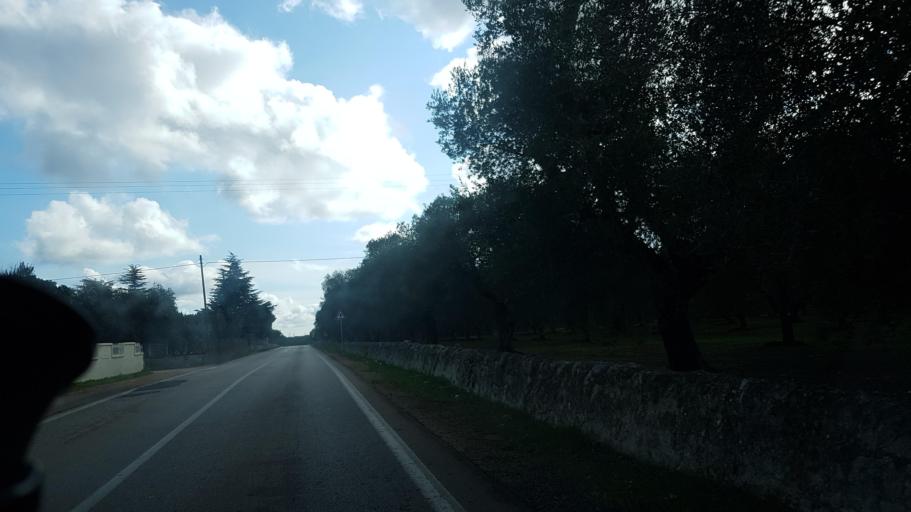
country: IT
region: Apulia
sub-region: Provincia di Brindisi
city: San Michele Salentino
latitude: 40.6648
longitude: 17.5993
